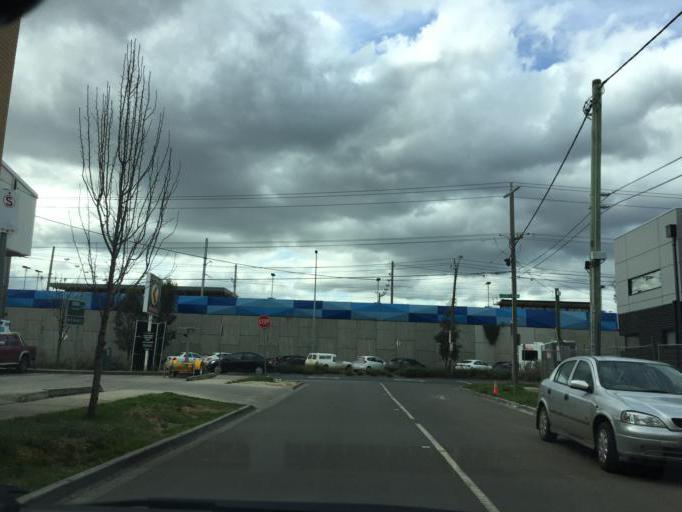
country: AU
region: Victoria
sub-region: Maribyrnong
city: West Footscray
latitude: -37.8001
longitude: 144.8634
